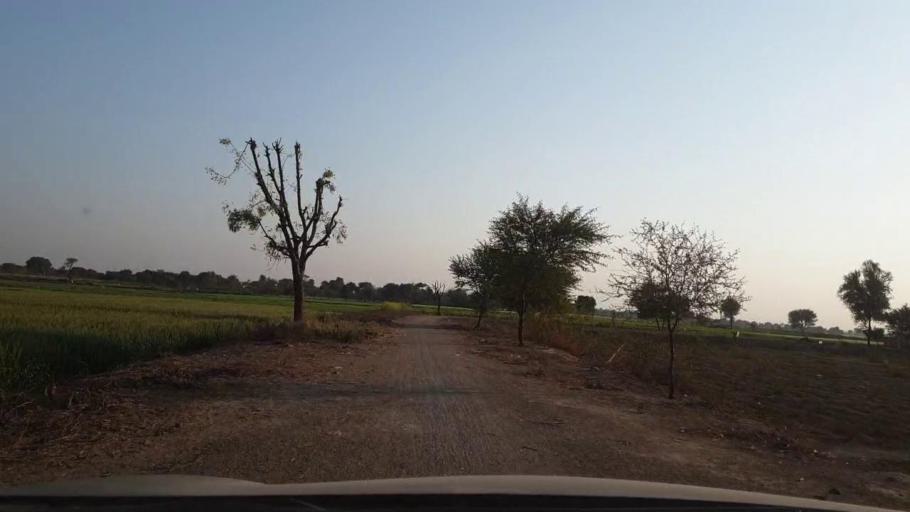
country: PK
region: Sindh
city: Tando Allahyar
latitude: 25.5651
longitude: 68.7916
